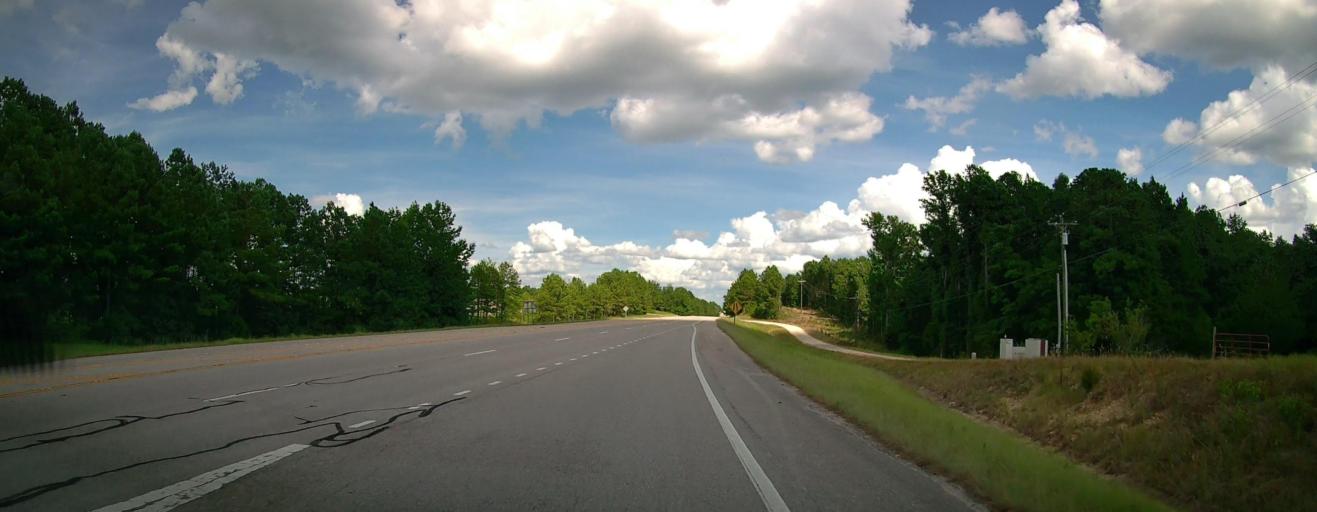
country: US
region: Alabama
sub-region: Macon County
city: Tuskegee
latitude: 32.4679
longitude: -85.5759
